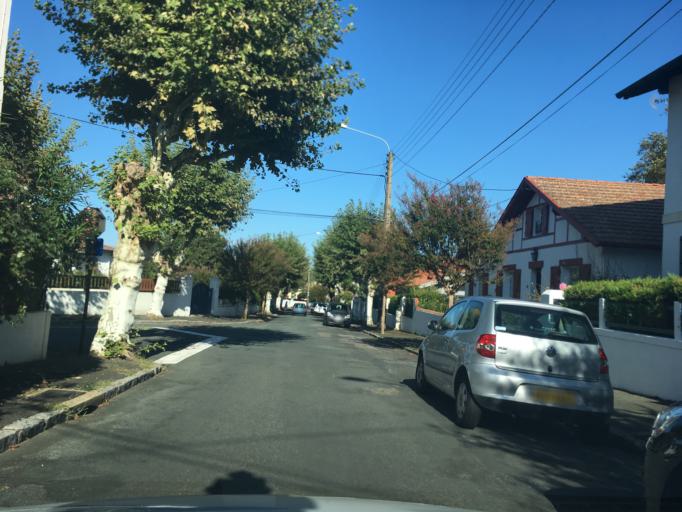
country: FR
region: Aquitaine
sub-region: Departement des Pyrenees-Atlantiques
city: Biarritz
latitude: 43.4683
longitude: -1.5520
